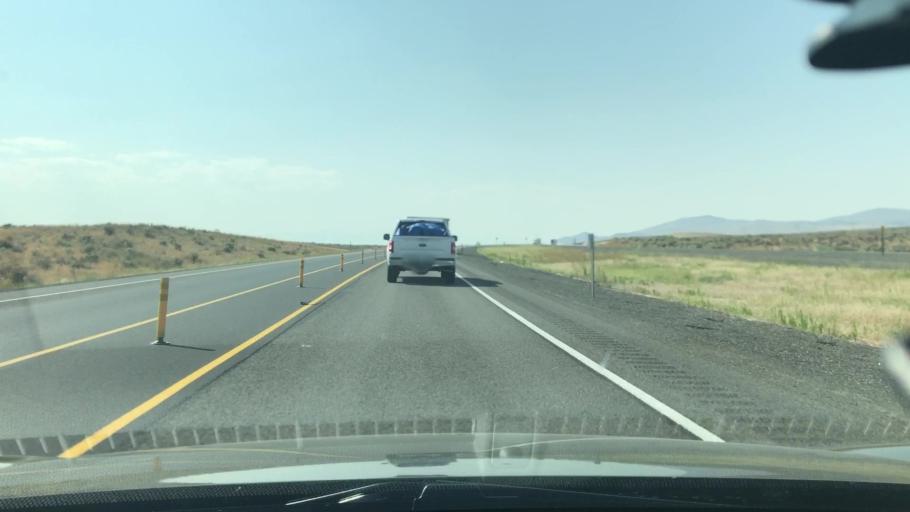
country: US
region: Oregon
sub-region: Baker County
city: Baker City
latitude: 44.6887
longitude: -117.6812
